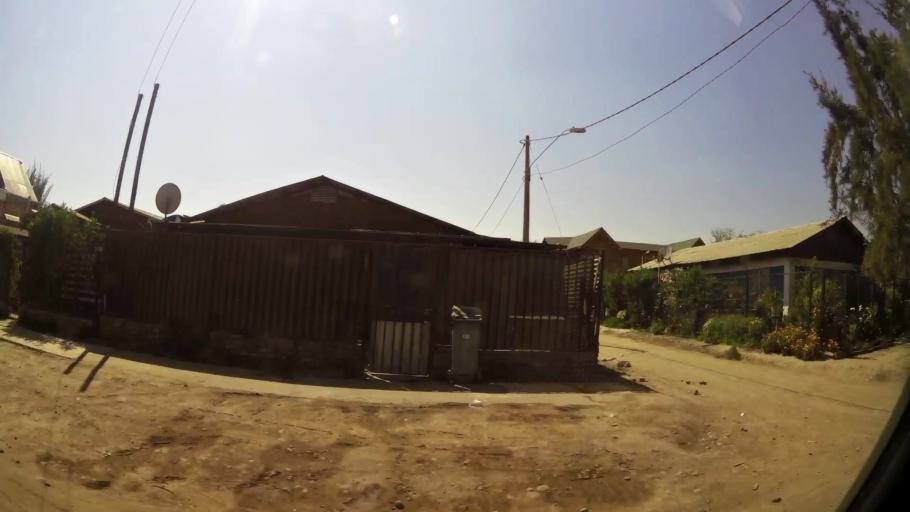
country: CL
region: Santiago Metropolitan
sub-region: Provincia de Talagante
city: Penaflor
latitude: -33.5841
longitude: -70.8182
